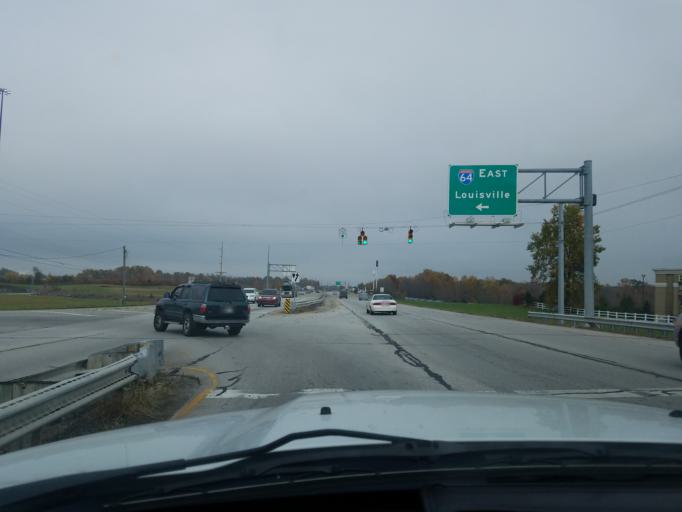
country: US
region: Indiana
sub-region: Harrison County
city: Corydon
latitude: 38.2377
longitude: -86.1270
